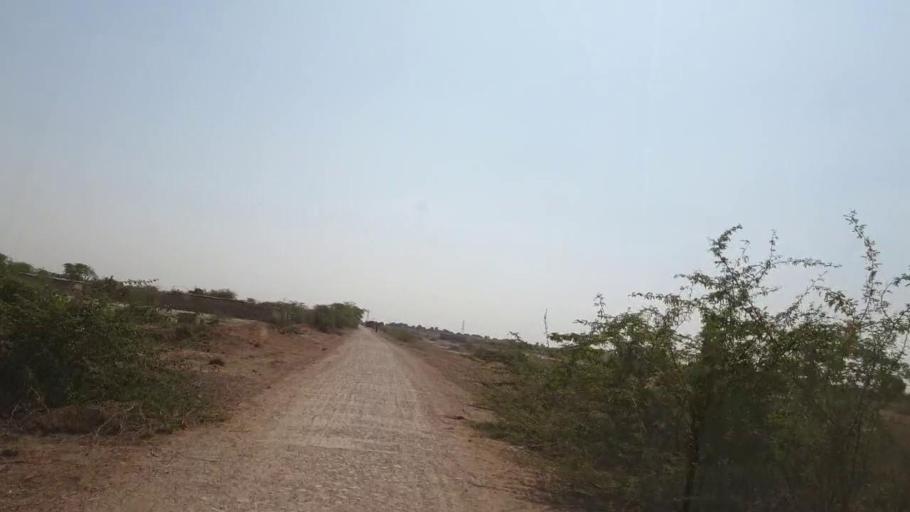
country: PK
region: Sindh
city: Nabisar
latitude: 25.0747
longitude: 69.5488
